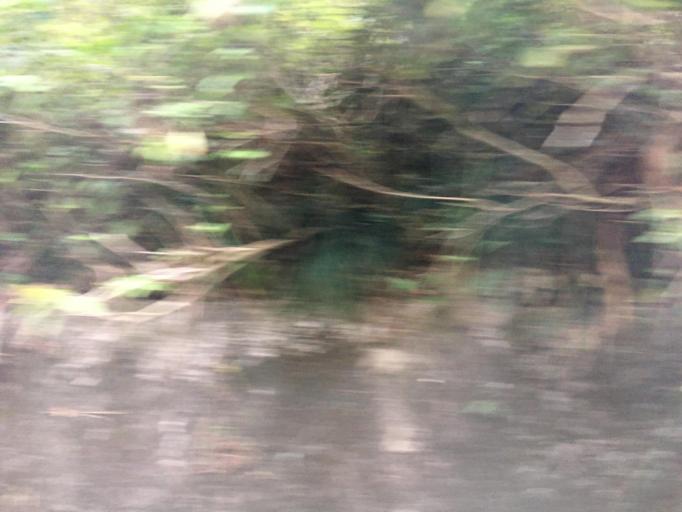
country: TW
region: Taiwan
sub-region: Chiayi
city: Jiayi Shi
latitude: 23.5414
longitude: 120.6069
